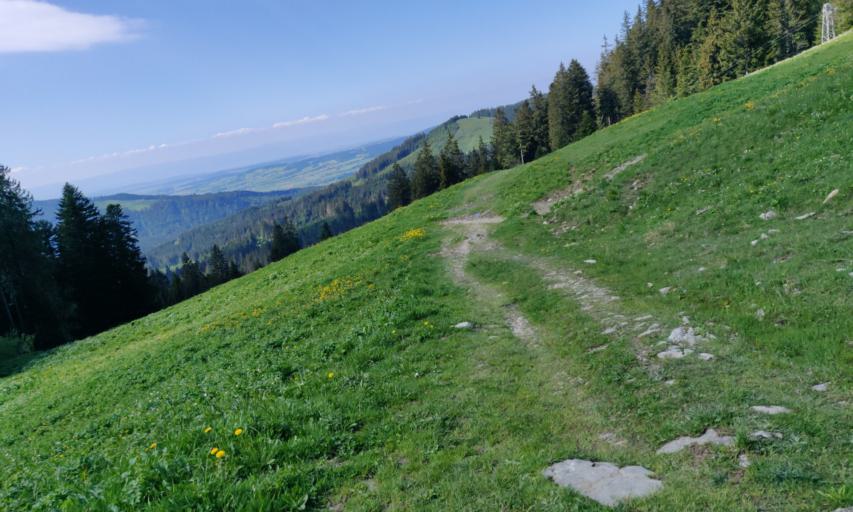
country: CH
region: Fribourg
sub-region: Gruyere District
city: Vuadens
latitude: 46.5561
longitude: 7.0201
